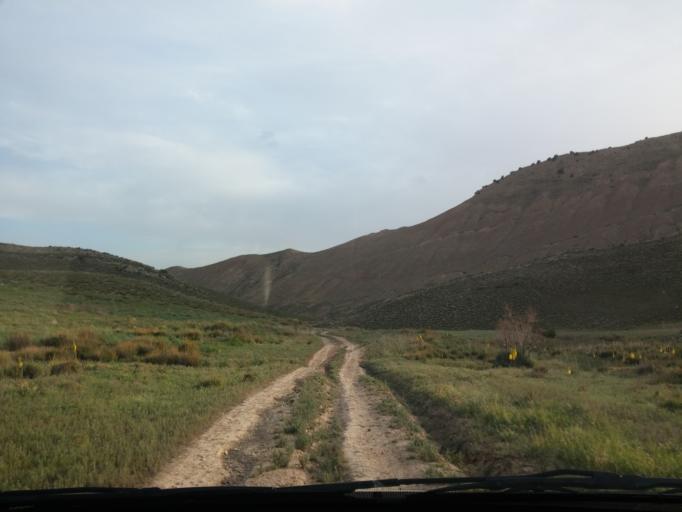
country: IR
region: Semnan
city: Istgah-e Rah Ahan-e Garmsar
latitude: 35.4866
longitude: 52.2955
